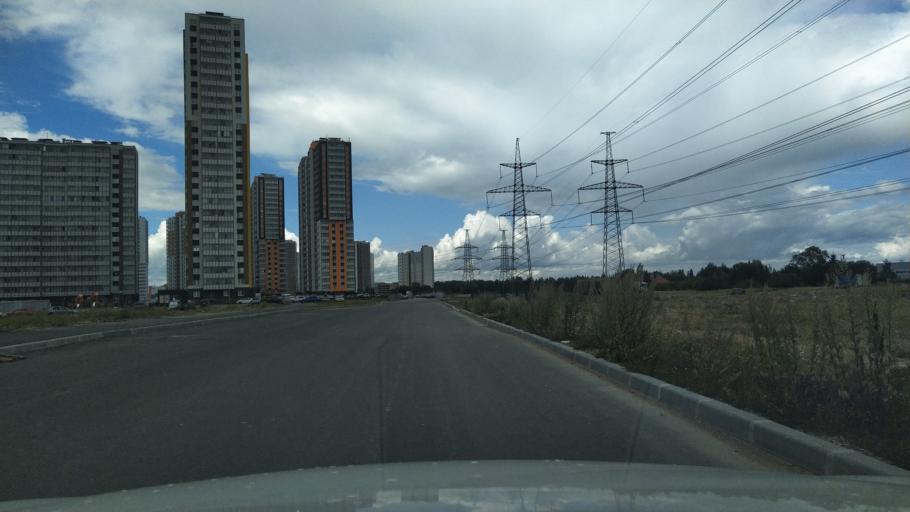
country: RU
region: St.-Petersburg
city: Krasnogvargeisky
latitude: 60.0057
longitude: 30.4834
